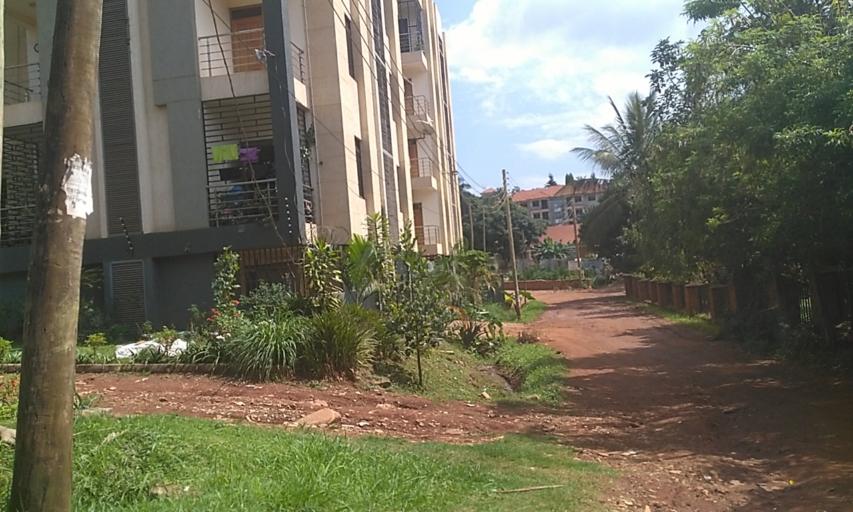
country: UG
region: Central Region
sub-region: Wakiso District
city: Kireka
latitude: 0.3461
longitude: 32.6131
